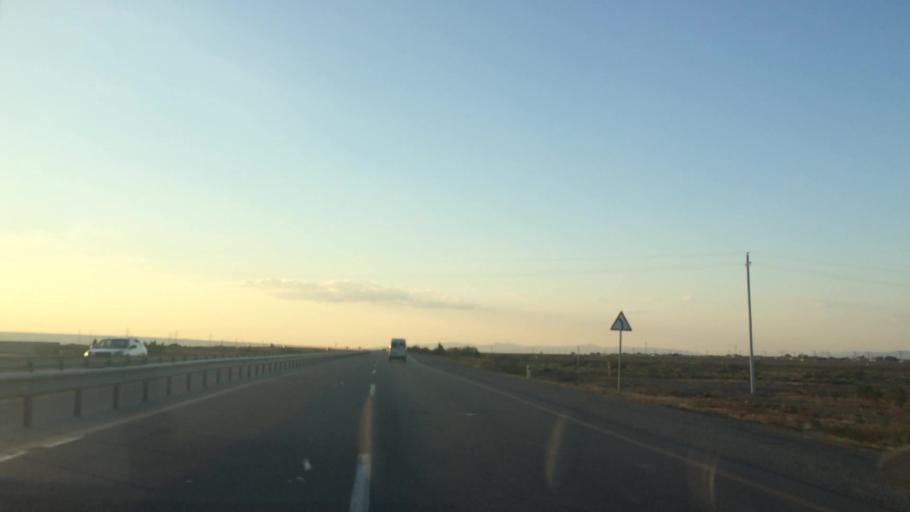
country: AZ
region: Baki
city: Qobustan
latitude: 39.9806
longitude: 49.2372
